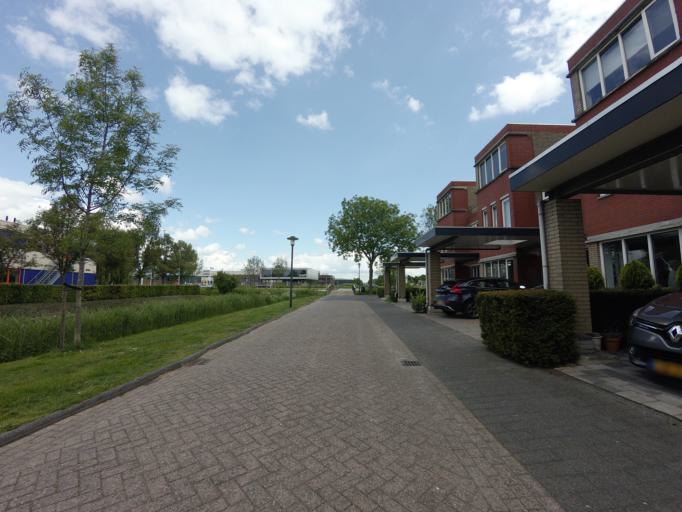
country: NL
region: North Brabant
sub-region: Gemeente Woudrichem
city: Woudrichem
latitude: 51.8381
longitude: 5.0034
